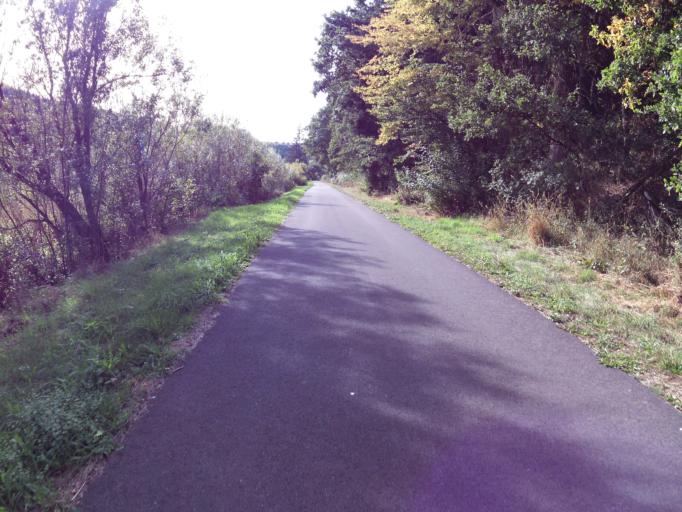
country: DE
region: Rheinland-Pfalz
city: Winterspelt
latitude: 50.2240
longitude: 6.2236
